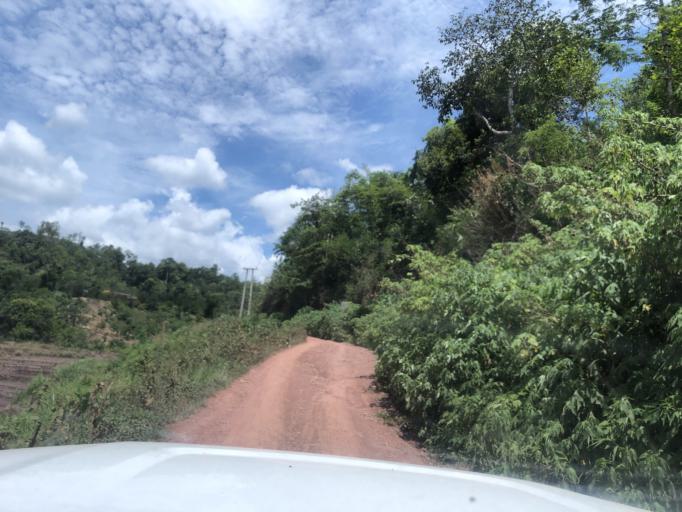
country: CN
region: Yunnan
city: Menglie
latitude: 22.2426
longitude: 101.6108
